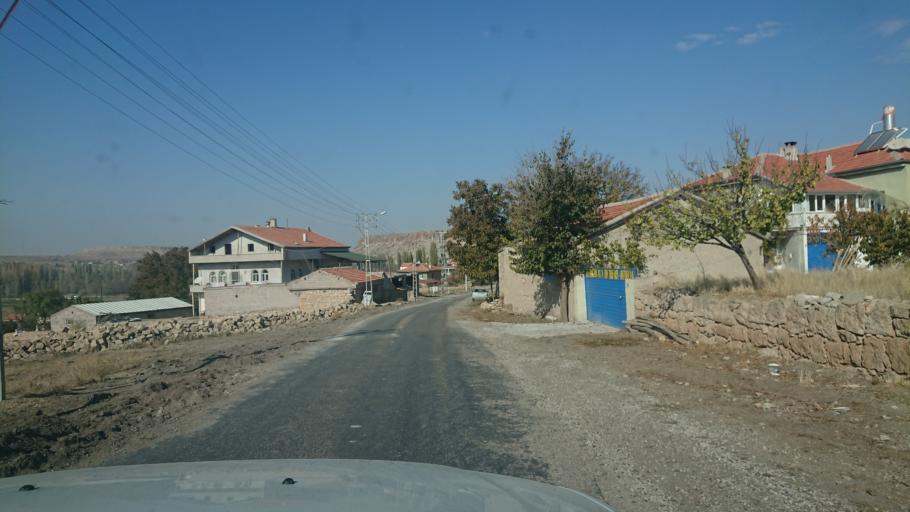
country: TR
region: Aksaray
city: Gulagac
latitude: 38.3479
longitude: 34.2362
